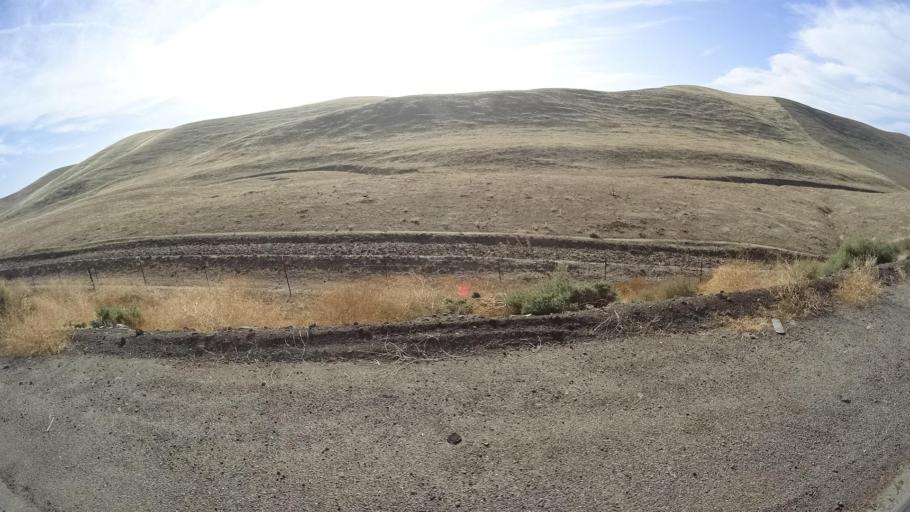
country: US
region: California
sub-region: Tulare County
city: Richgrove
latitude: 35.6229
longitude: -119.0087
